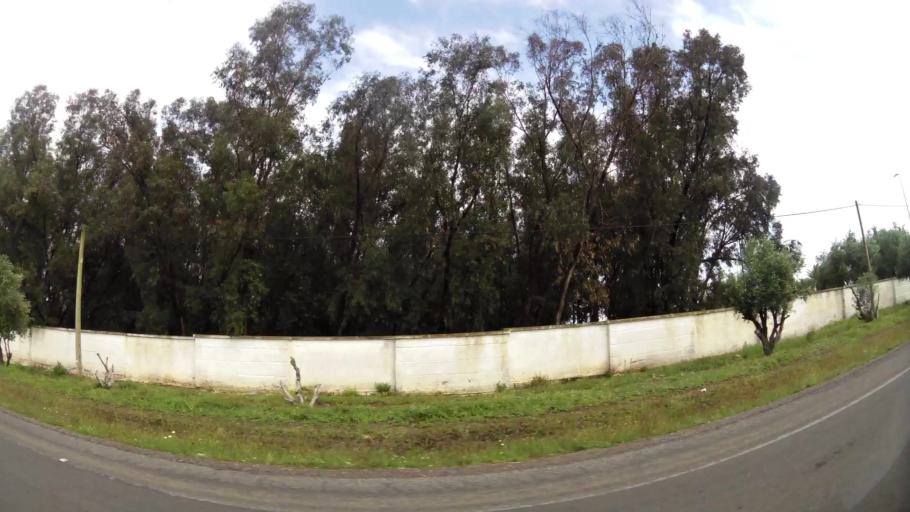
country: MA
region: Rabat-Sale-Zemmour-Zaer
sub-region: Khemisset
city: Khemisset
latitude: 33.7985
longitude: -6.0985
